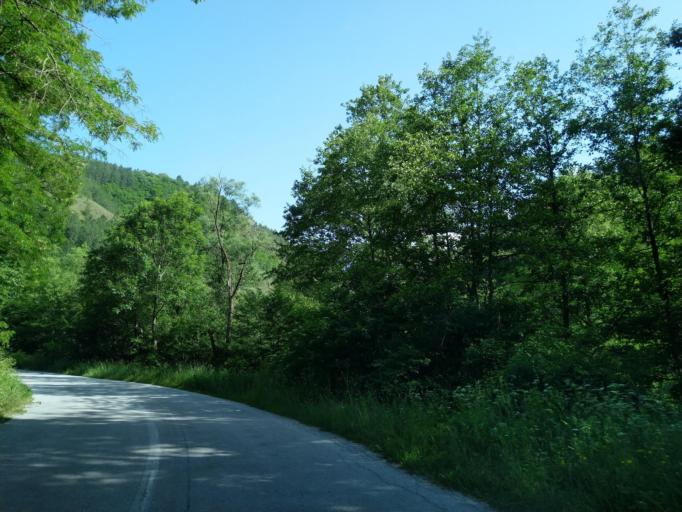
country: RS
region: Central Serbia
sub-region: Zlatiborski Okrug
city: Bajina Basta
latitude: 43.8557
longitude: 19.6223
